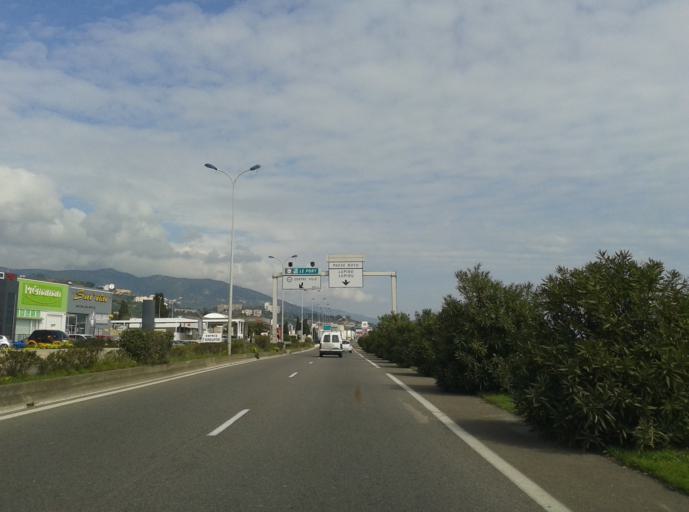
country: FR
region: Corsica
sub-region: Departement de la Haute-Corse
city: Bastia
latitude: 42.6727
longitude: 9.4438
